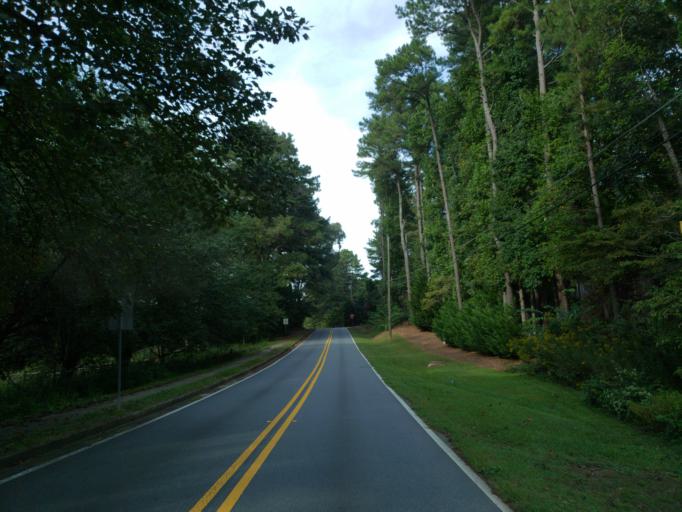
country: US
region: Georgia
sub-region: Cherokee County
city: Woodstock
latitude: 34.0566
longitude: -84.4979
